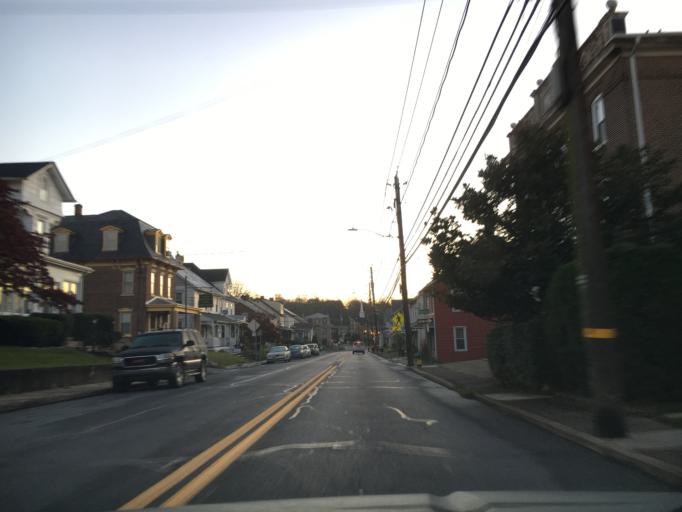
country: US
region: Pennsylvania
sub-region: Lehigh County
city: Egypt
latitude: 40.6799
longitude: -75.5323
